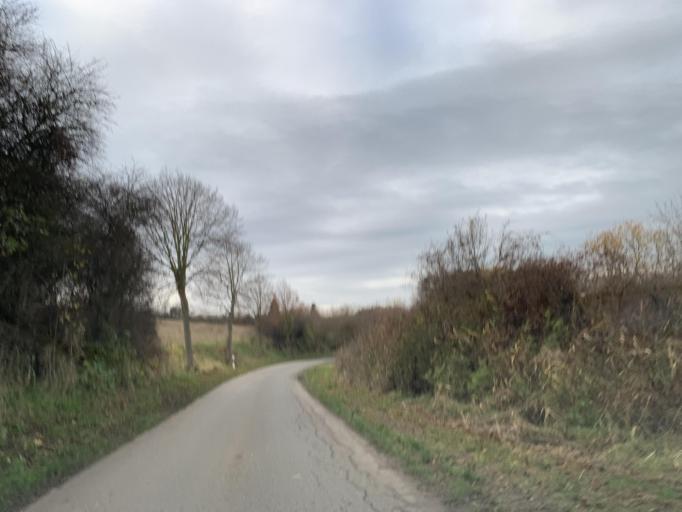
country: DE
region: Mecklenburg-Vorpommern
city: Carpin
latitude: 53.4015
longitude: 13.2034
